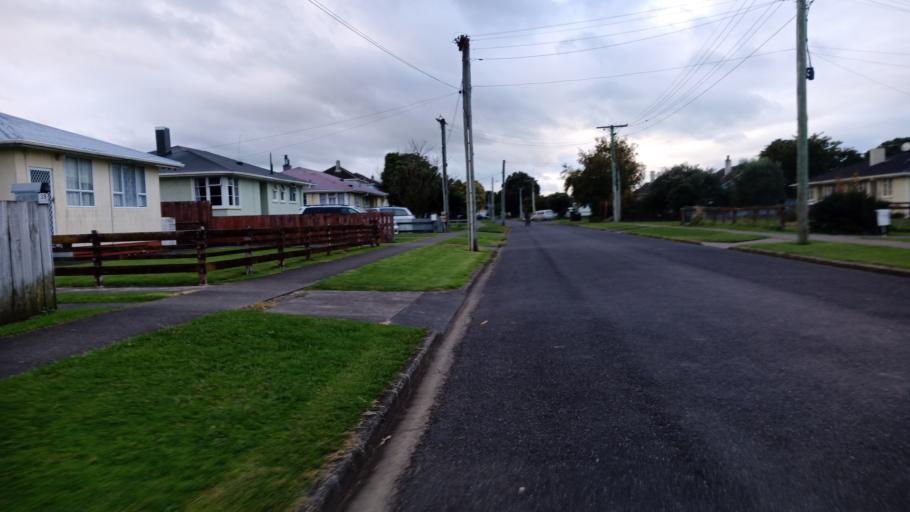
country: NZ
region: Gisborne
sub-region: Gisborne District
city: Gisborne
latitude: -38.6561
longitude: 177.9999
